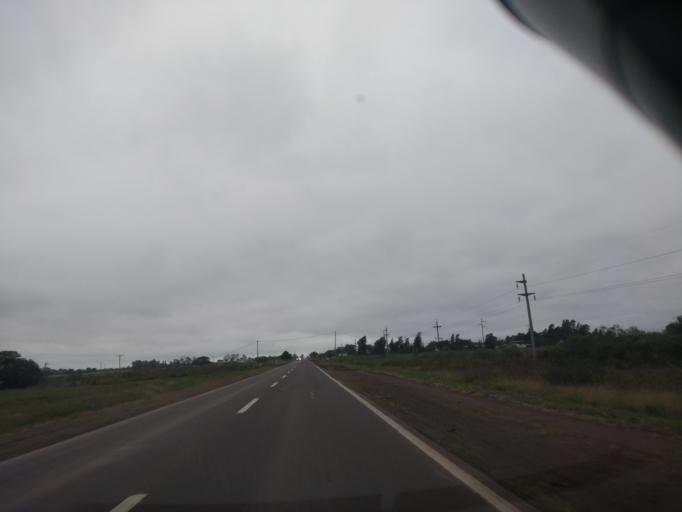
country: AR
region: Chaco
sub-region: Departamento de Quitilipi
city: Quitilipi
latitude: -26.8706
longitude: -60.2542
